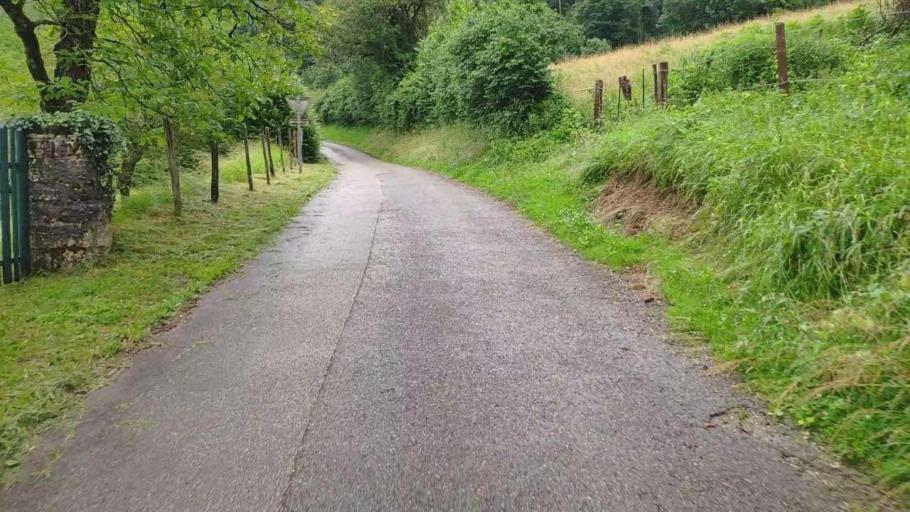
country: FR
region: Franche-Comte
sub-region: Departement du Jura
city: Poligny
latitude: 46.7827
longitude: 5.6179
